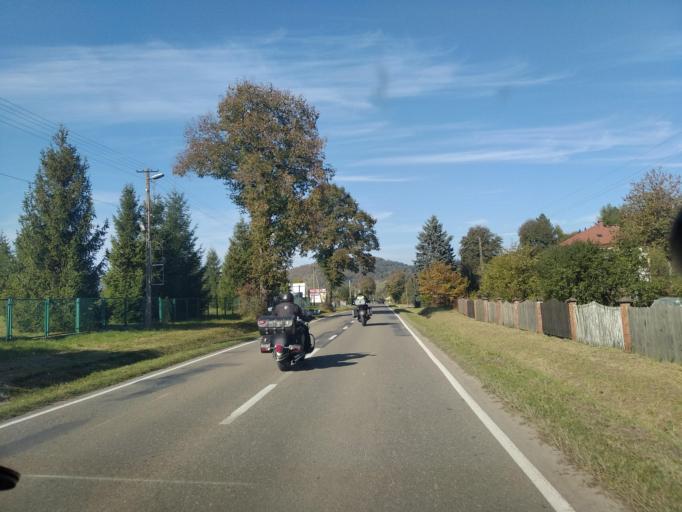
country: PL
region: Subcarpathian Voivodeship
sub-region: Powiat leski
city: Baligrod
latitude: 49.3463
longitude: 22.2897
